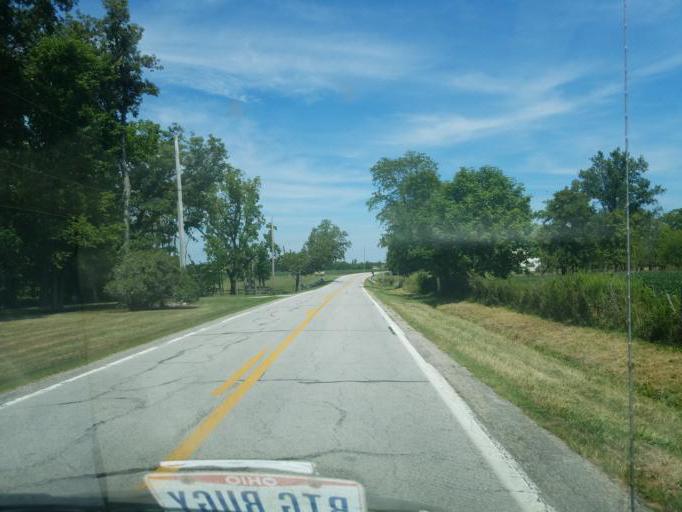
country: US
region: Ohio
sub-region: Madison County
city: West Jefferson
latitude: 39.8432
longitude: -83.2305
